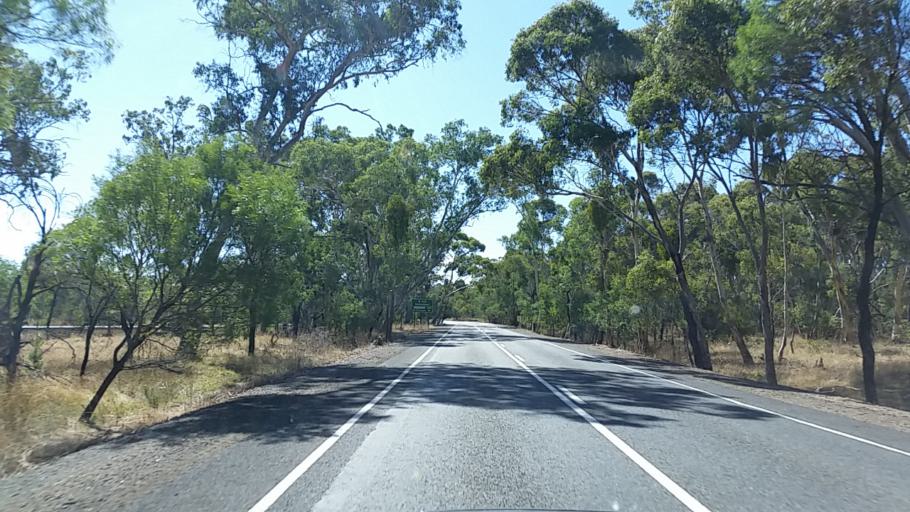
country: AU
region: South Australia
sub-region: Adelaide Hills
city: Birdwood
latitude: -34.7361
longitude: 138.9619
